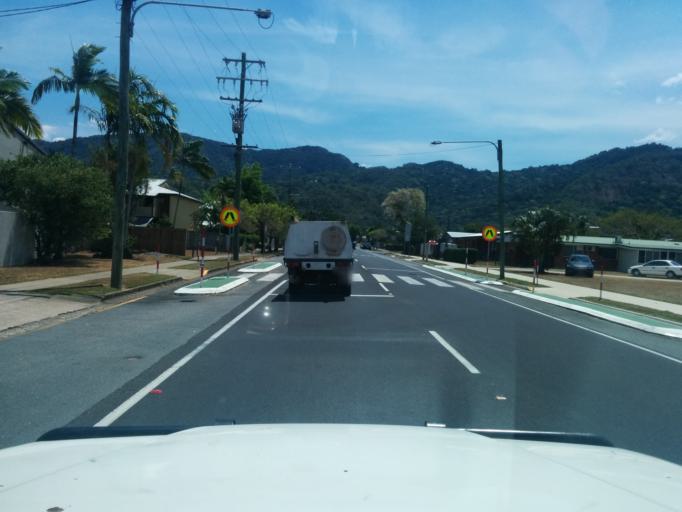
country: AU
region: Queensland
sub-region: Cairns
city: Woree
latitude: -16.9431
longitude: 145.7374
